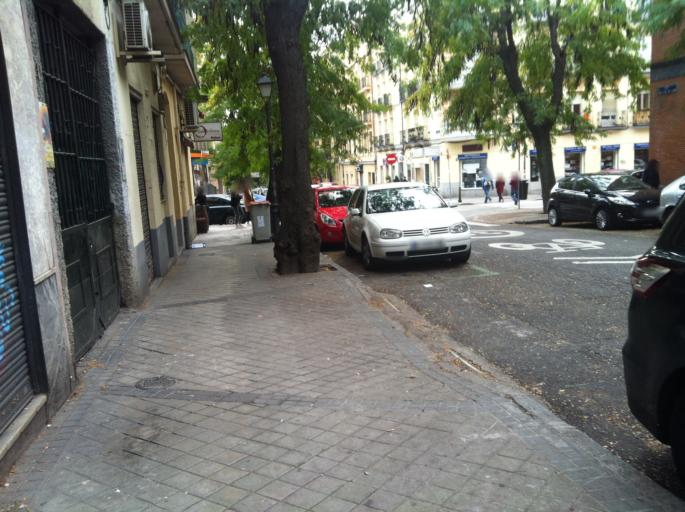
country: ES
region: Madrid
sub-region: Provincia de Madrid
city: Arganzuela
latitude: 40.4050
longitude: -3.6992
